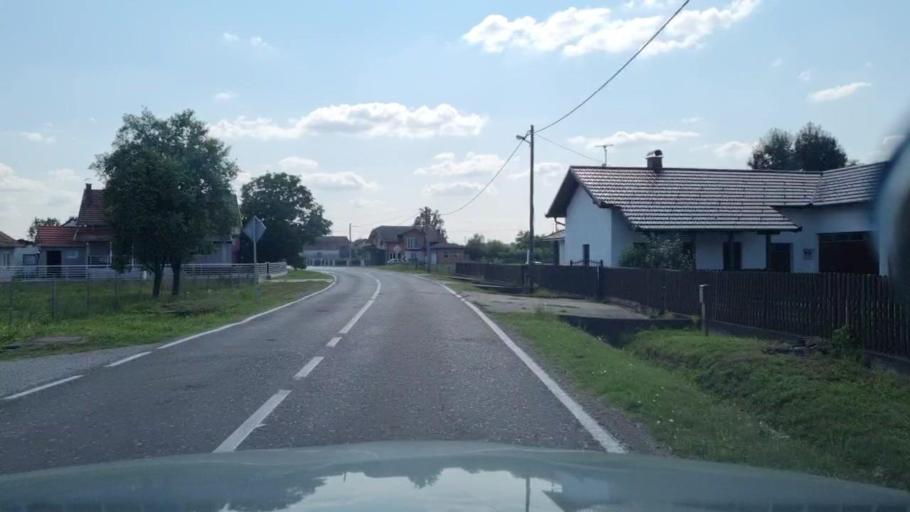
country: BA
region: Federation of Bosnia and Herzegovina
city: Odzak
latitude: 45.0366
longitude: 18.3681
